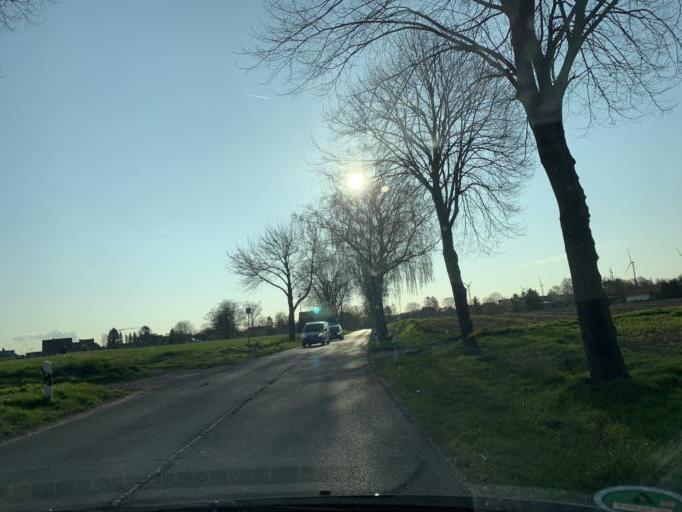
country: DE
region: North Rhine-Westphalia
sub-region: Regierungsbezirk Koln
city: Titz
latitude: 50.9573
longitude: 6.4596
